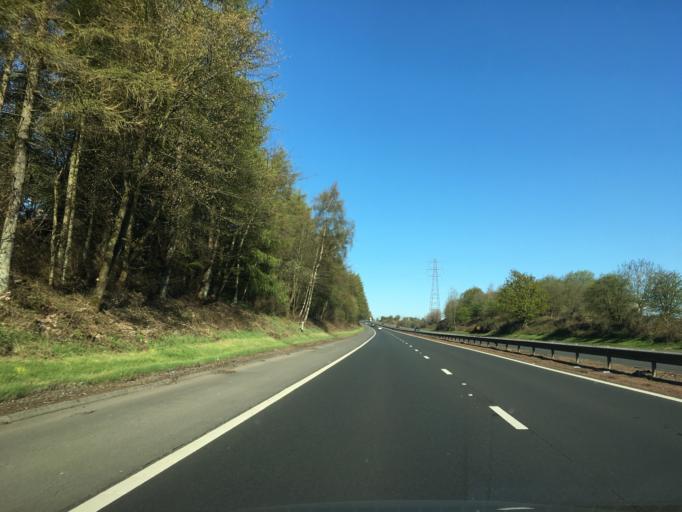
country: GB
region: Scotland
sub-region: Stirling
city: Cowie
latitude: 56.0633
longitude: -3.8628
